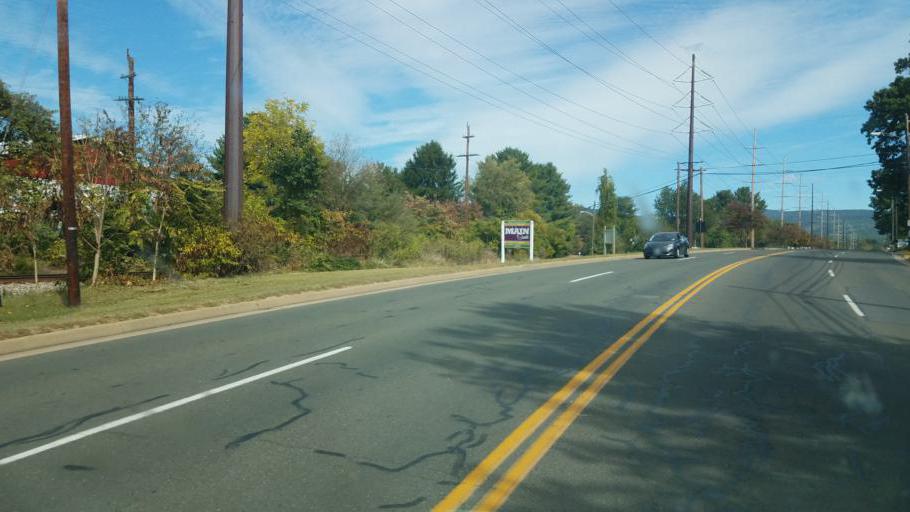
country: US
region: Virginia
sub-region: Page County
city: Luray
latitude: 38.6695
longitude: -78.4337
